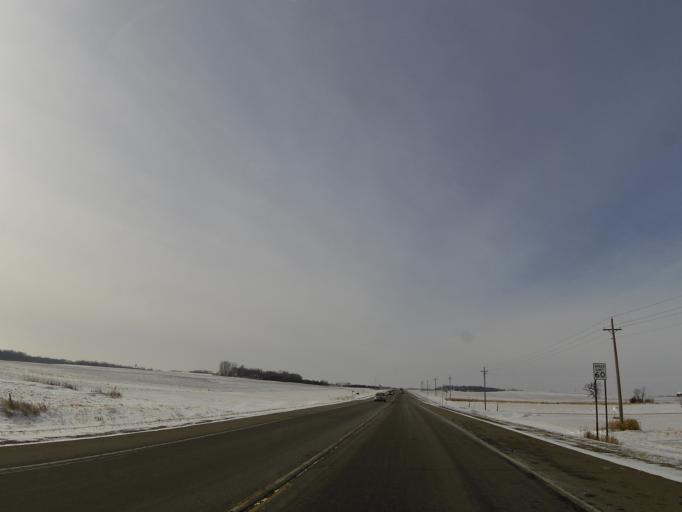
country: US
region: Minnesota
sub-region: McLeod County
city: Lester Prairie
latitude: 44.9068
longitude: -93.9806
